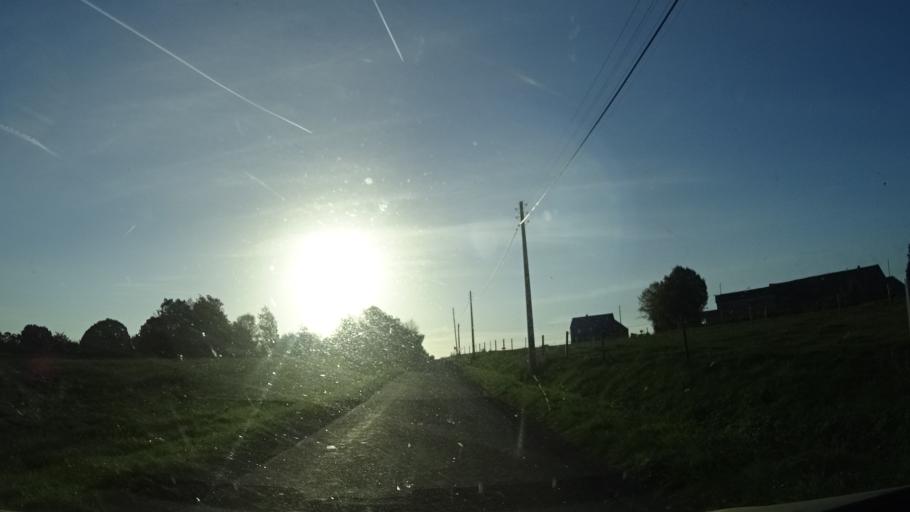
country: BE
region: Wallonia
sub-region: Province du Hainaut
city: Beaumont
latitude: 50.2579
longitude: 4.2419
